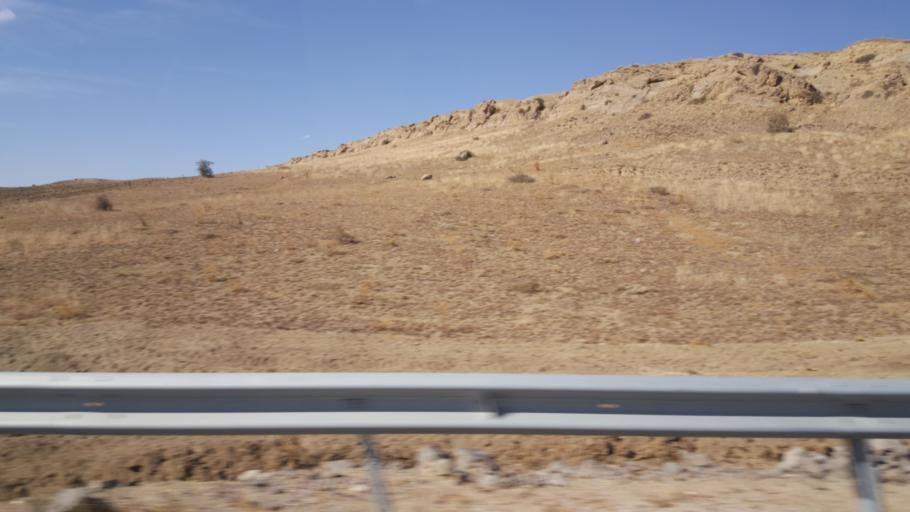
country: TR
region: Ankara
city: Haymana
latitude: 39.4767
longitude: 32.5476
